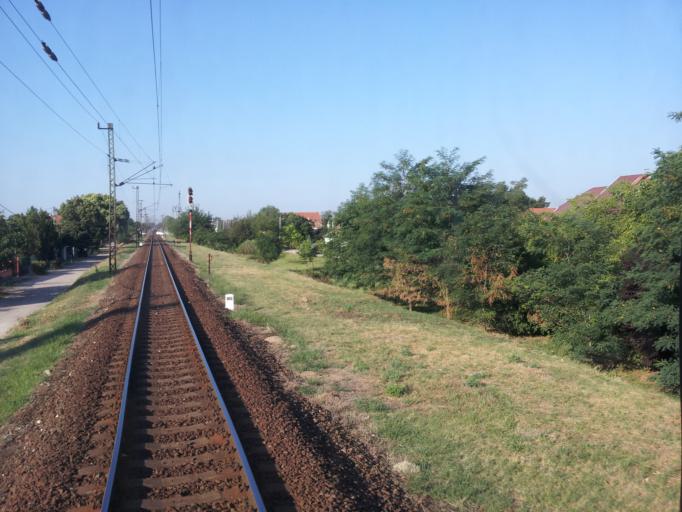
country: HU
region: Pest
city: Dunaharaszti
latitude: 47.3591
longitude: 19.1018
